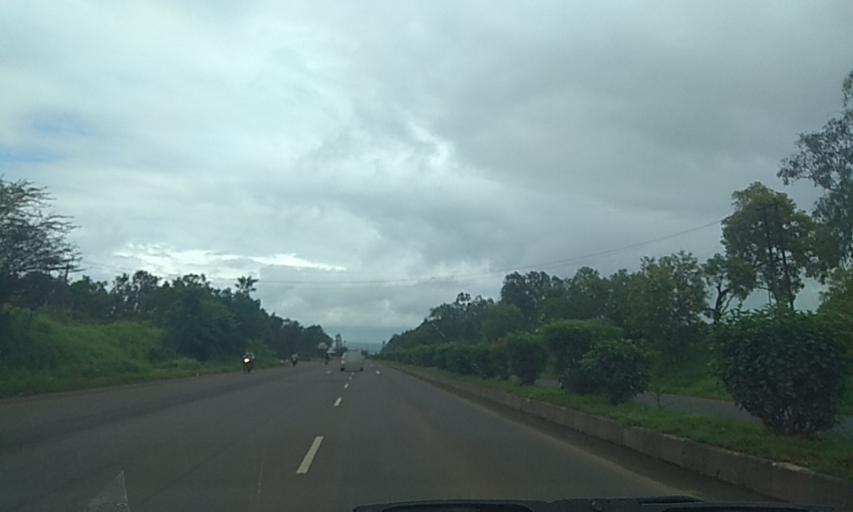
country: IN
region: Karnataka
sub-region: Belgaum
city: Belgaum
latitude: 15.8881
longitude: 74.5242
